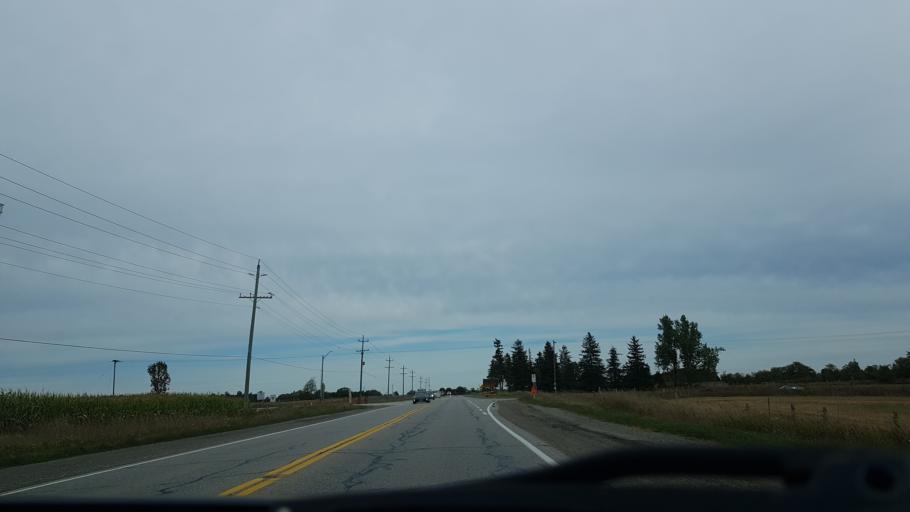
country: CA
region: Ontario
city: Orangeville
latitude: 43.8200
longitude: -80.0401
